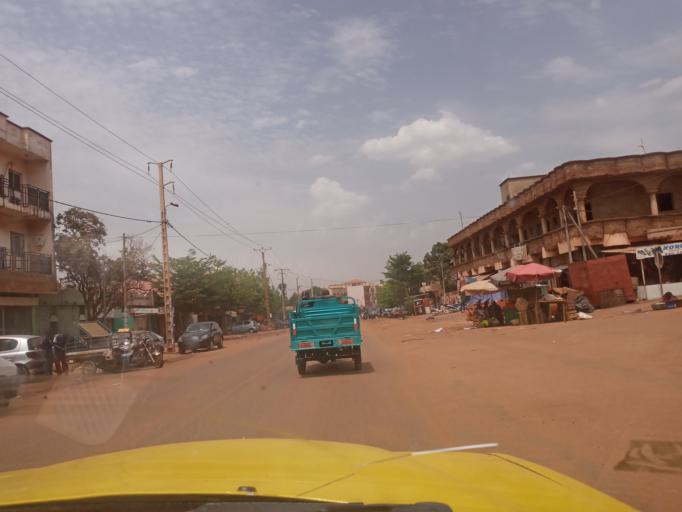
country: ML
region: Bamako
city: Bamako
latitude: 12.6092
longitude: -7.9587
